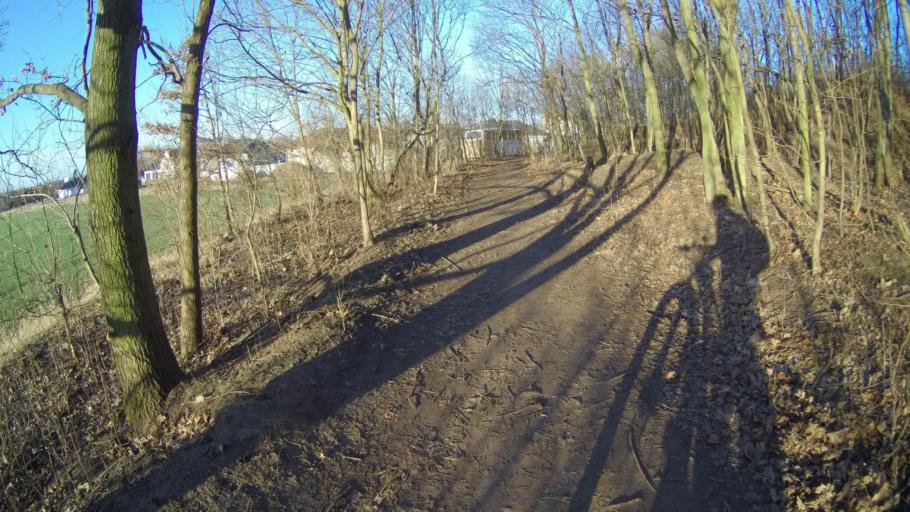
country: CZ
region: Central Bohemia
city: Neratovice
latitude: 50.2351
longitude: 14.5070
